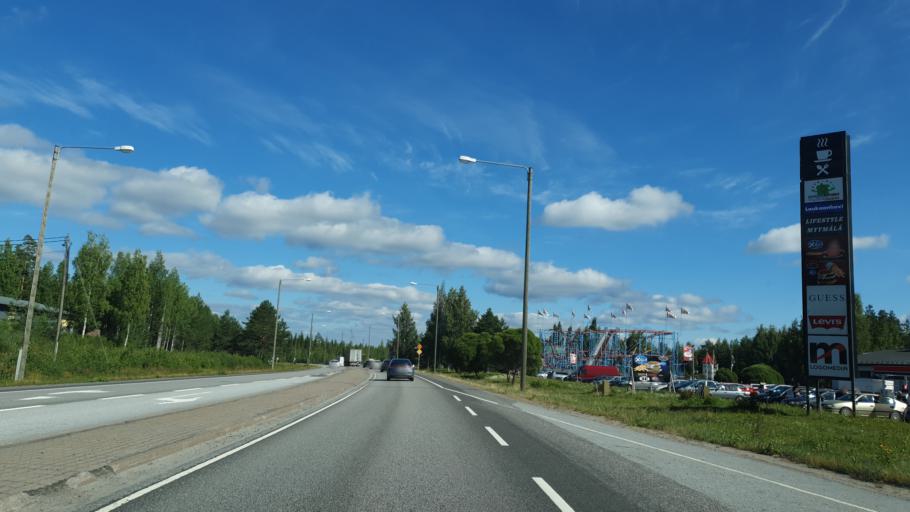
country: FI
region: Central Finland
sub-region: Jyvaeskylae
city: Toivakka
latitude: 62.2467
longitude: 26.1358
